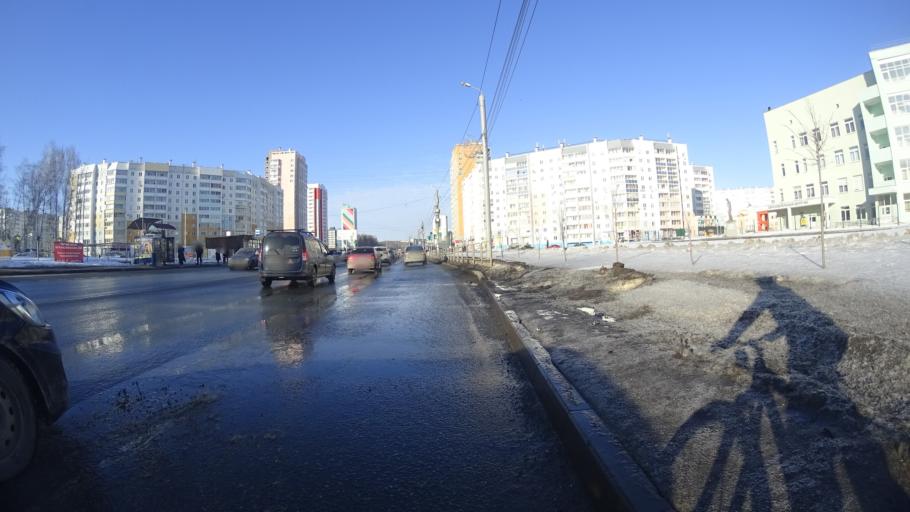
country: RU
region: Chelyabinsk
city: Roshchino
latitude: 55.2064
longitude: 61.2845
